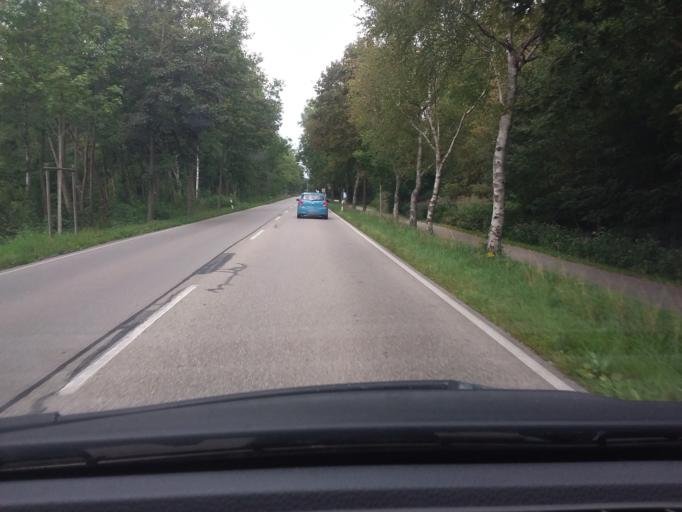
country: DE
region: Bavaria
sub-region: Upper Bavaria
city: Hebertshausen
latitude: 48.2546
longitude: 11.4945
